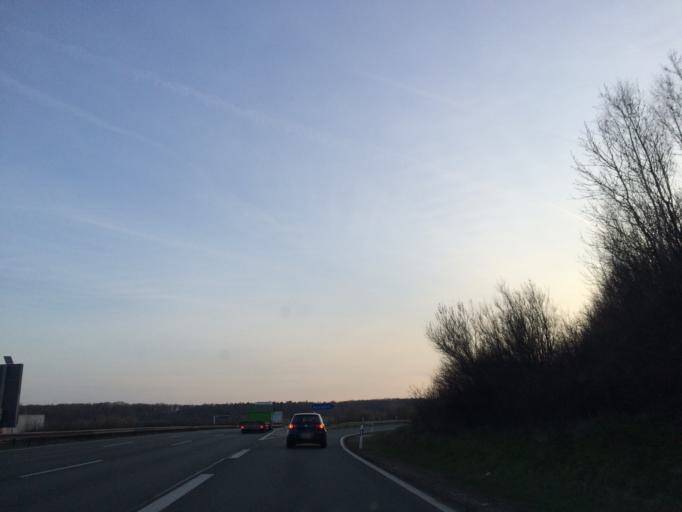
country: DE
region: Thuringia
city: Petersberg
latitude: 50.9681
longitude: 11.8612
